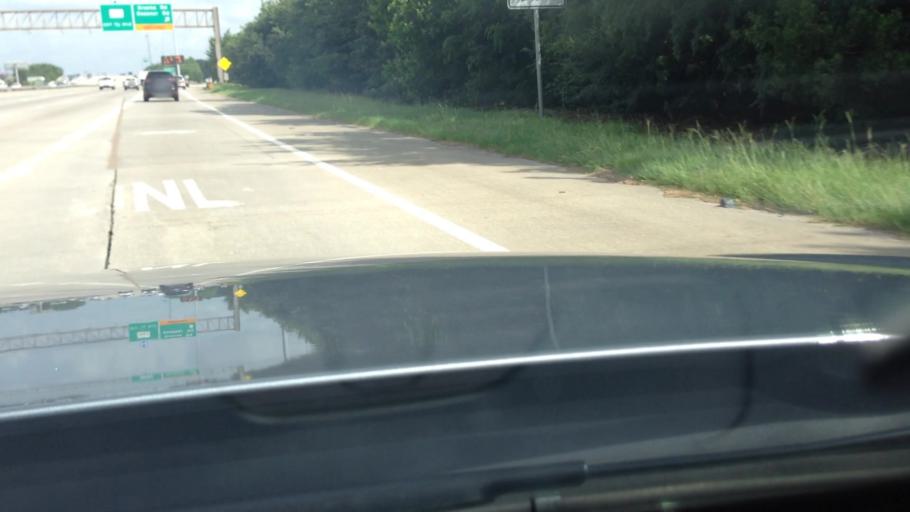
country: US
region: Texas
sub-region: Harris County
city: Hudson
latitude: 29.9493
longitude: -95.5319
